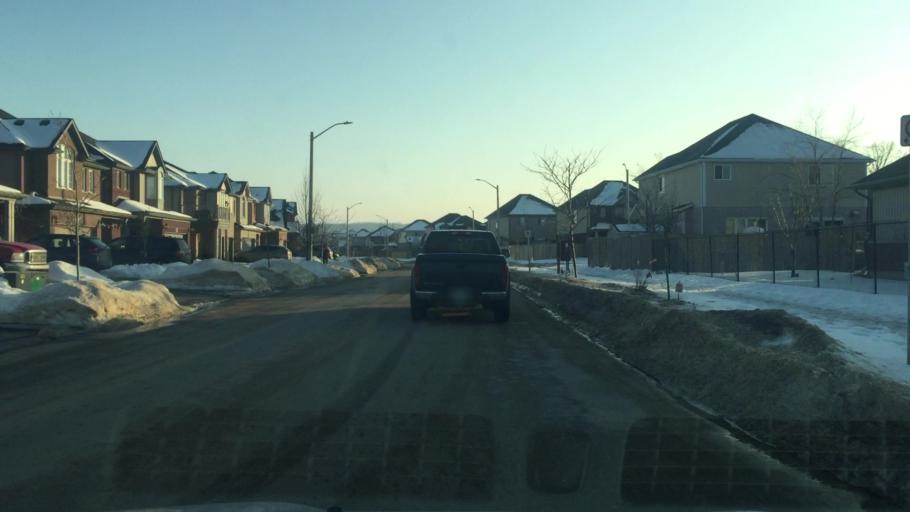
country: CA
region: Ontario
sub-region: Regional Municipality of Niagara
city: St. Catharines
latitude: 43.1753
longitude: -79.4703
